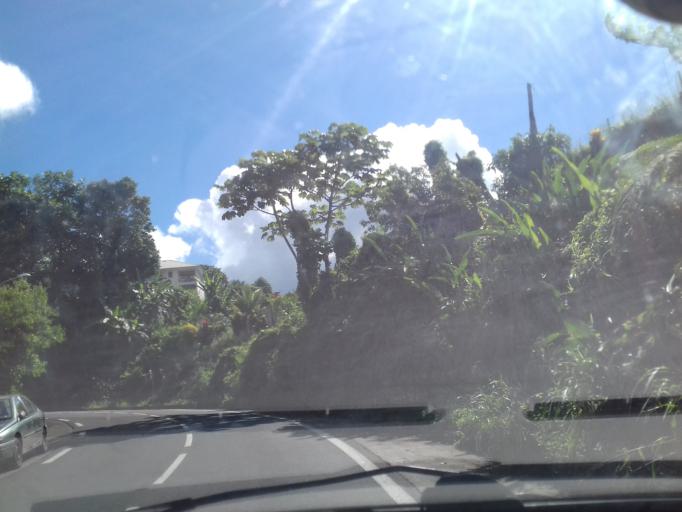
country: MQ
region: Martinique
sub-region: Martinique
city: Le Gros-Morne
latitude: 14.7130
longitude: -61.0114
